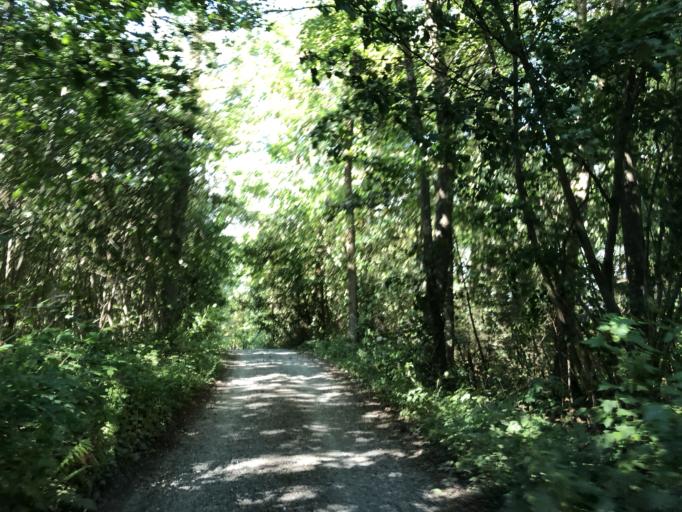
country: DK
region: South Denmark
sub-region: Vejle Kommune
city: Brejning
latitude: 55.6886
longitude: 9.6639
